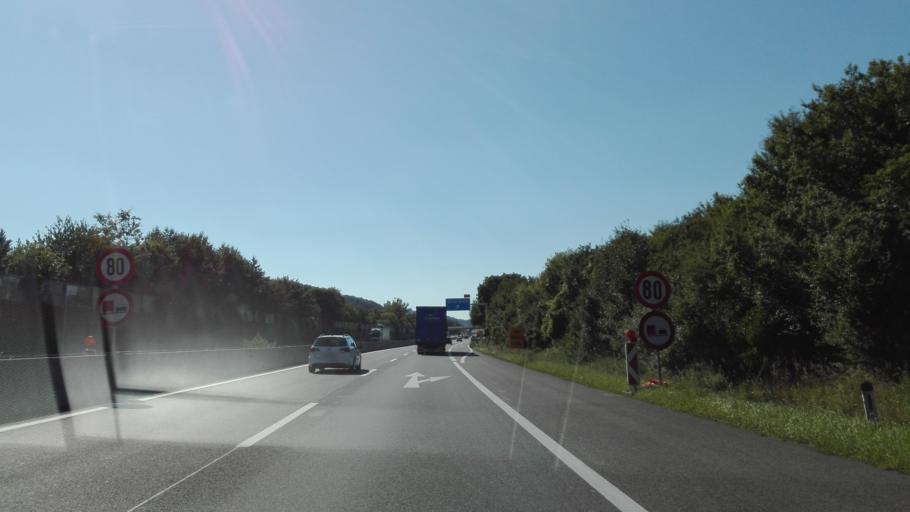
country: AT
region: Lower Austria
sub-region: Politischer Bezirk Modling
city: Gaaden
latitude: 48.0717
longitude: 16.1935
